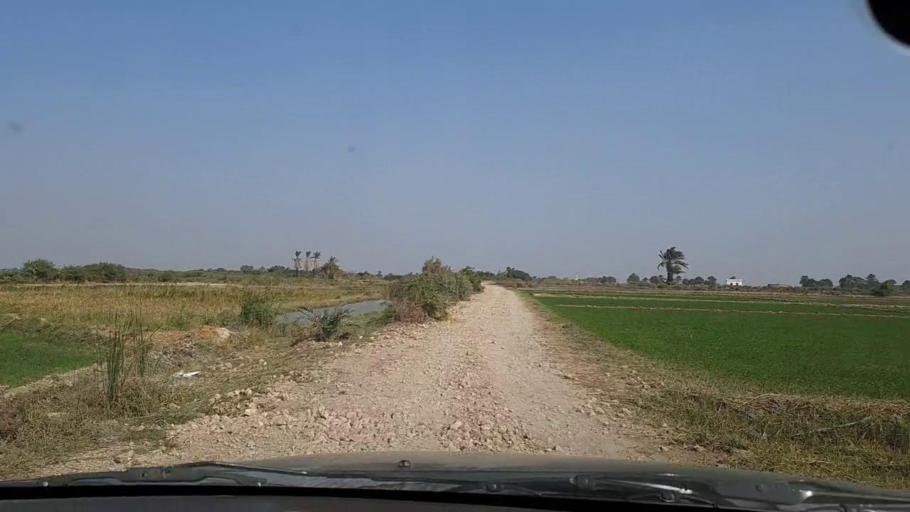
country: PK
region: Sindh
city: Mirpur Sakro
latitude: 24.3777
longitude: 67.6833
